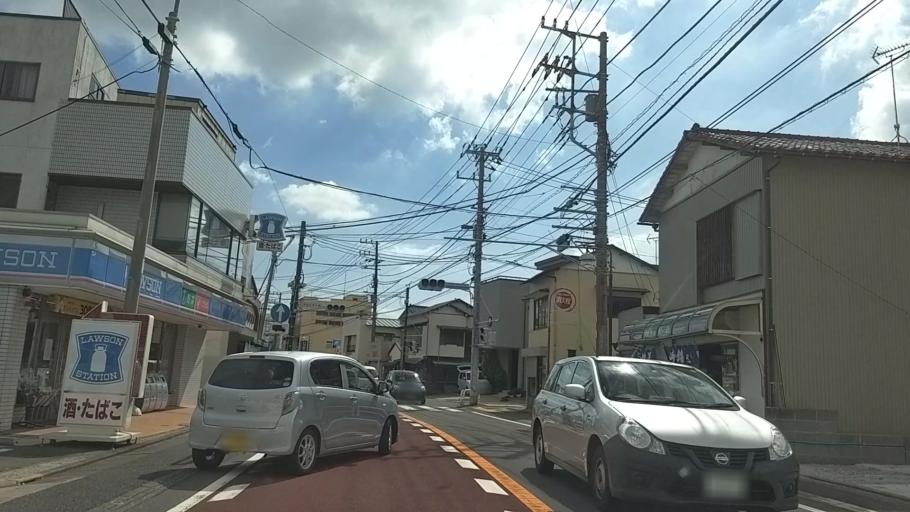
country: JP
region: Kanagawa
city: Miura
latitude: 35.1479
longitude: 139.6256
